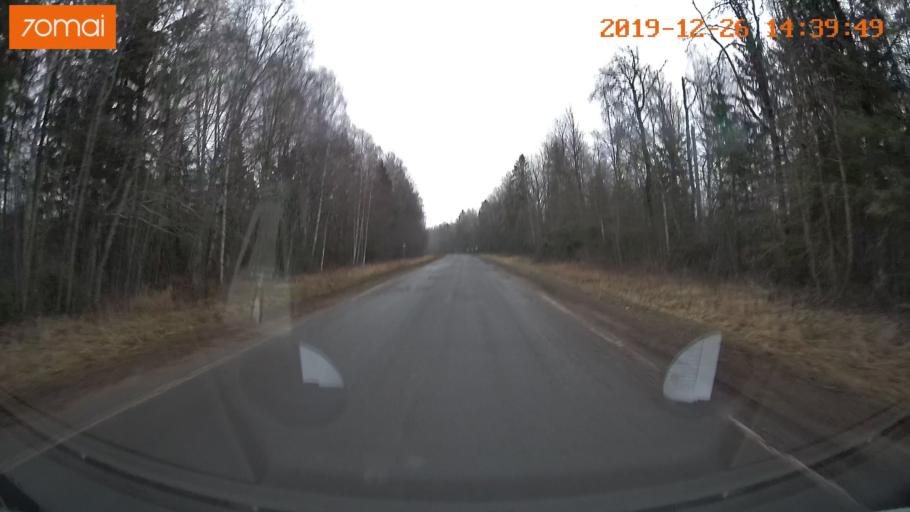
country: RU
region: Jaroslavl
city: Poshekhon'ye
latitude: 58.3798
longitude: 38.9861
